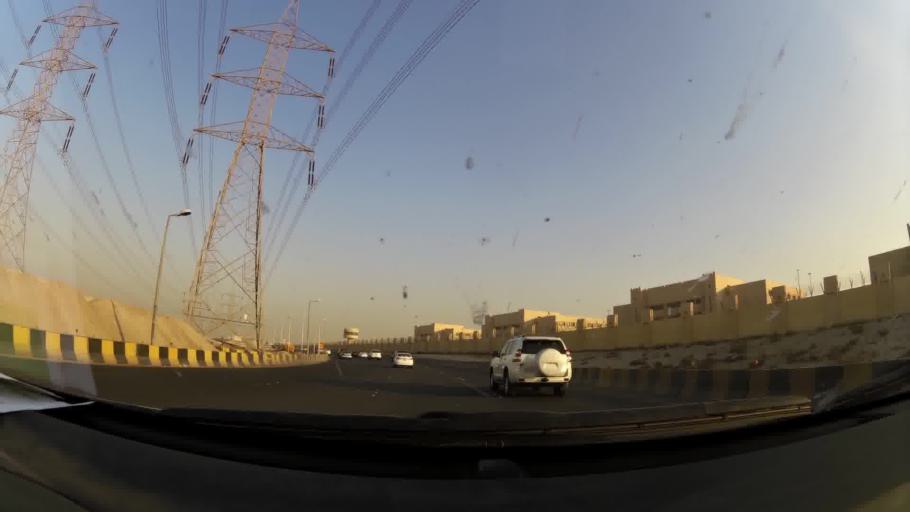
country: KW
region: Al Asimah
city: Ar Rabiyah
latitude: 29.2943
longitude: 47.8570
